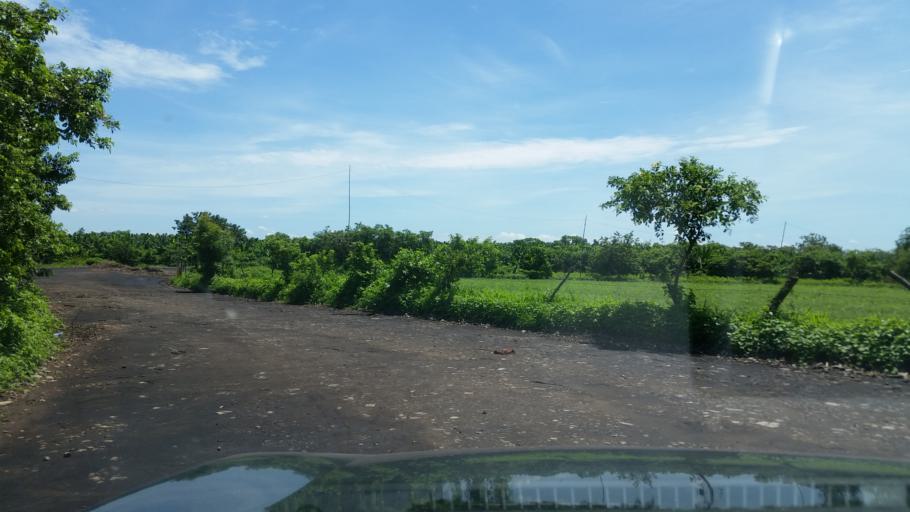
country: NI
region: Chinandega
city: Puerto Morazan
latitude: 12.7641
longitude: -87.1214
